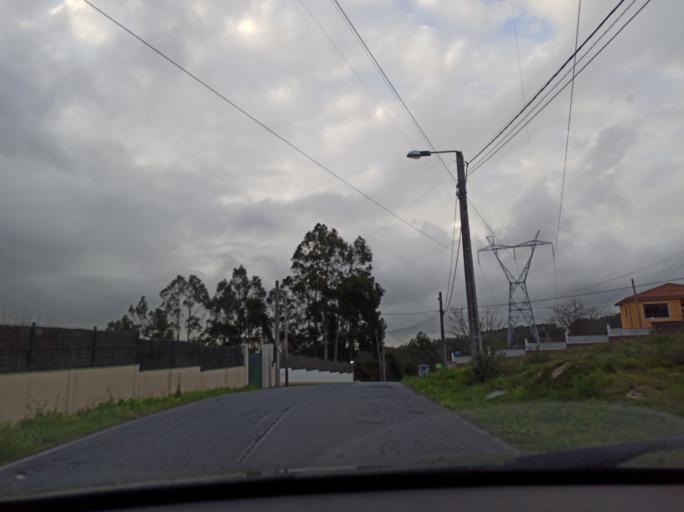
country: ES
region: Galicia
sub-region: Provincia da Coruna
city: Culleredo
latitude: 43.2992
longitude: -8.4325
